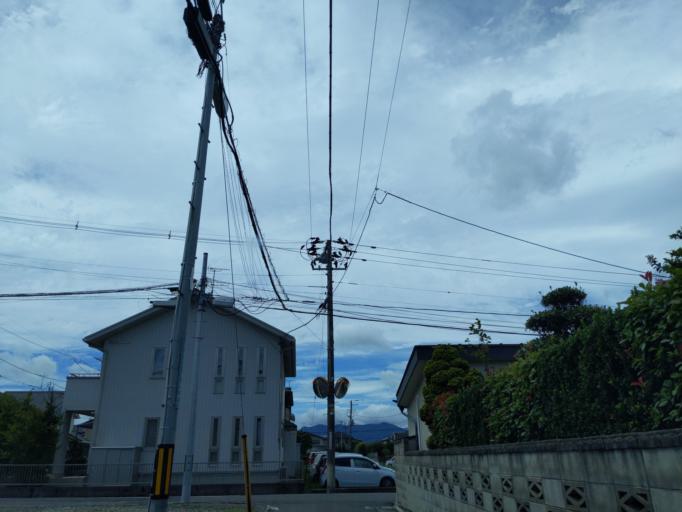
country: JP
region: Fukushima
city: Koriyama
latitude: 37.4046
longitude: 140.3465
